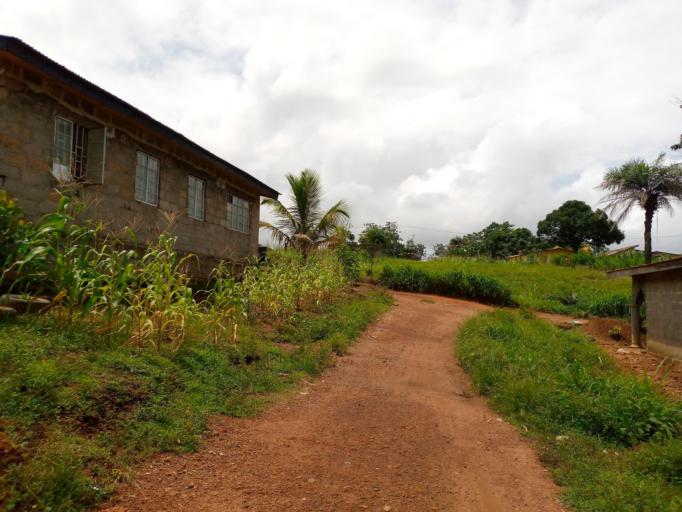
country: SL
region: Northern Province
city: Magburaka
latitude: 8.7273
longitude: -11.9357
